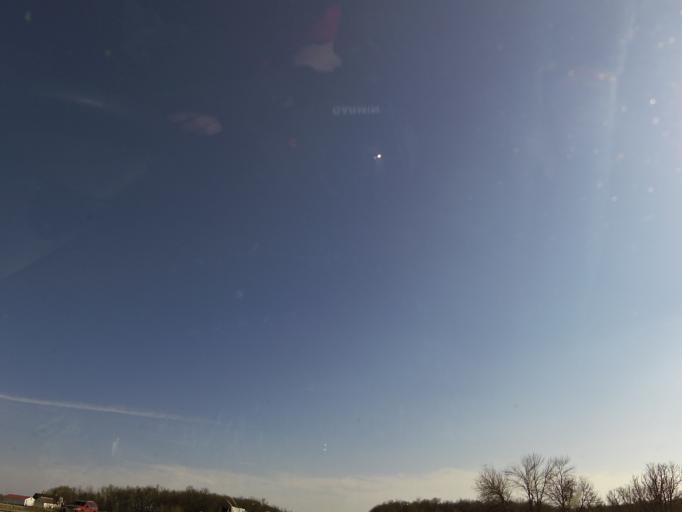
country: US
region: Minnesota
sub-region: Steele County
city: Owatonna
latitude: 44.0413
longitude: -93.2490
